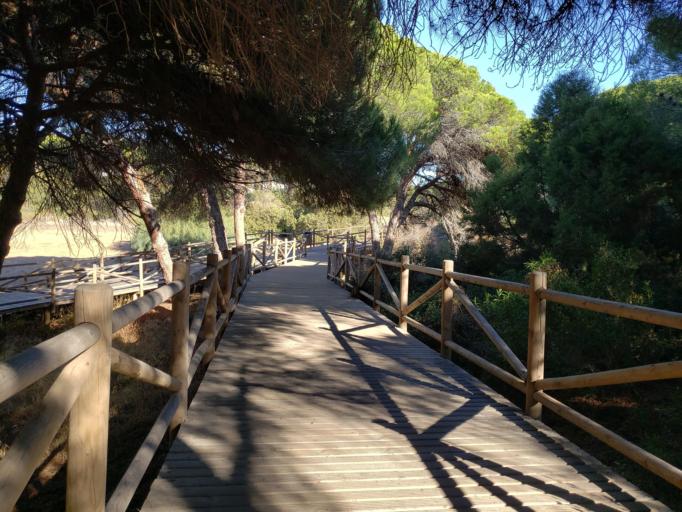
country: ES
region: Andalusia
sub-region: Provincia de Malaga
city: Ojen
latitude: 36.4871
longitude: -4.7491
